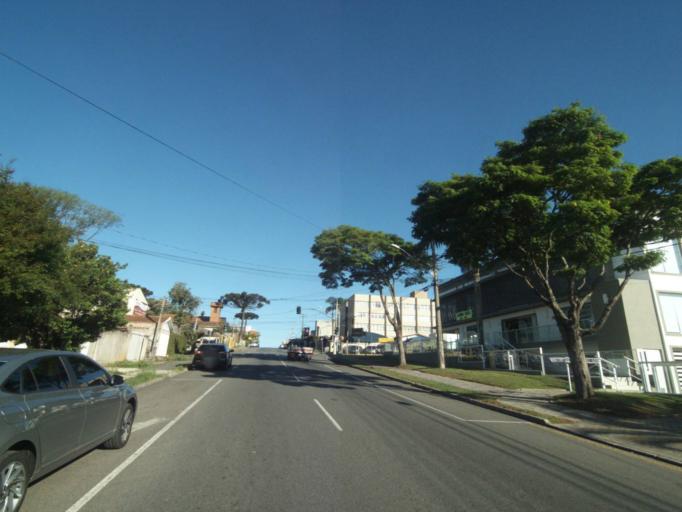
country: BR
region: Parana
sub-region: Curitiba
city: Curitiba
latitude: -25.3972
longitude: -49.2511
